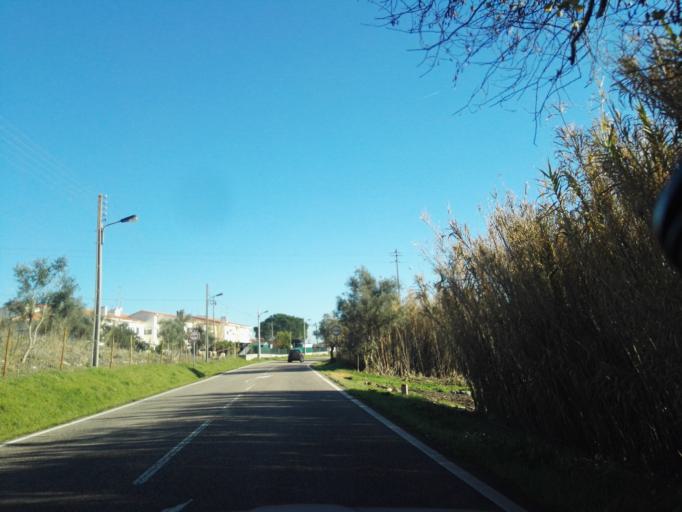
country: PT
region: Santarem
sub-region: Constancia
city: Constancia
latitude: 39.4823
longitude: -8.3044
